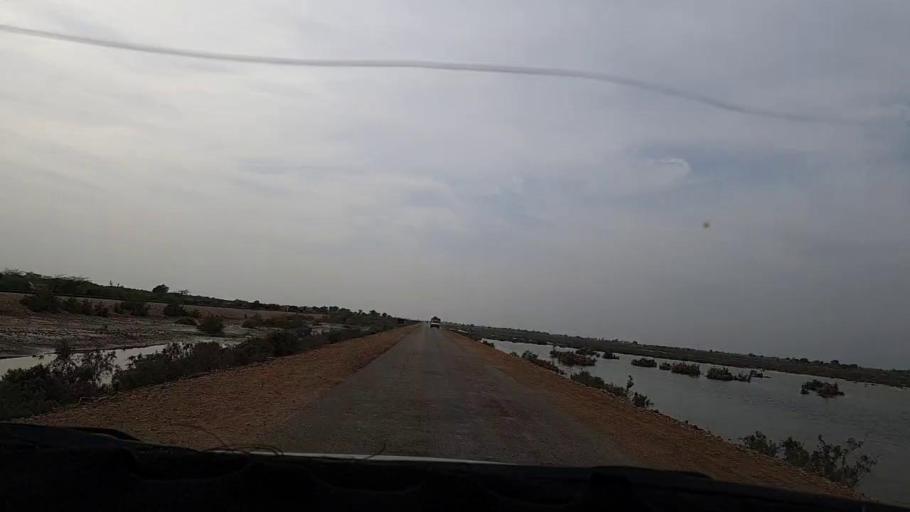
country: PK
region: Sindh
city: Pithoro
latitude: 25.5157
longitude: 69.2909
